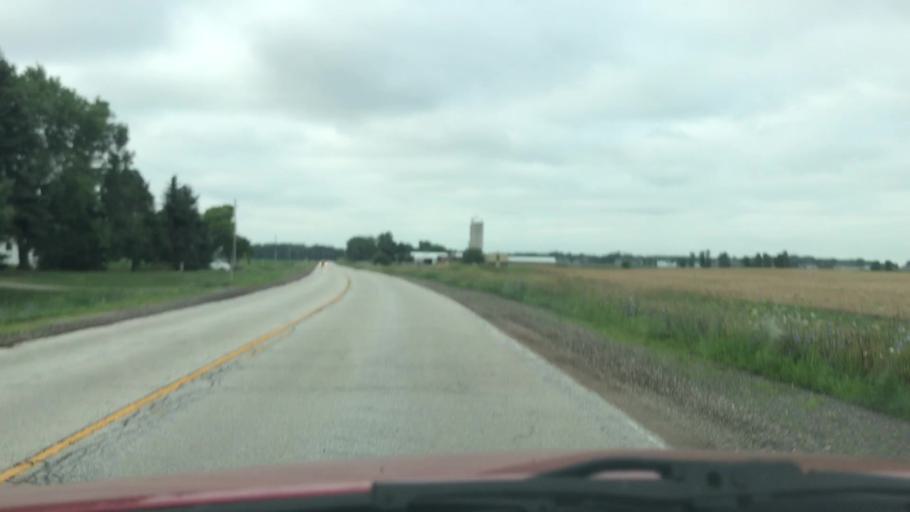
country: US
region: Wisconsin
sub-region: Brown County
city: De Pere
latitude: 44.4377
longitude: -88.1360
